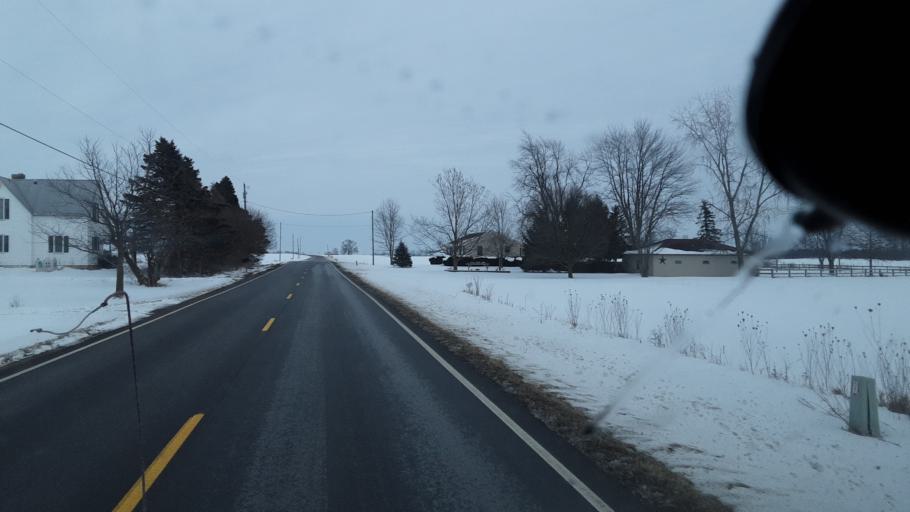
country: US
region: Ohio
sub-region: Union County
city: New California
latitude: 40.2125
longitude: -83.2304
